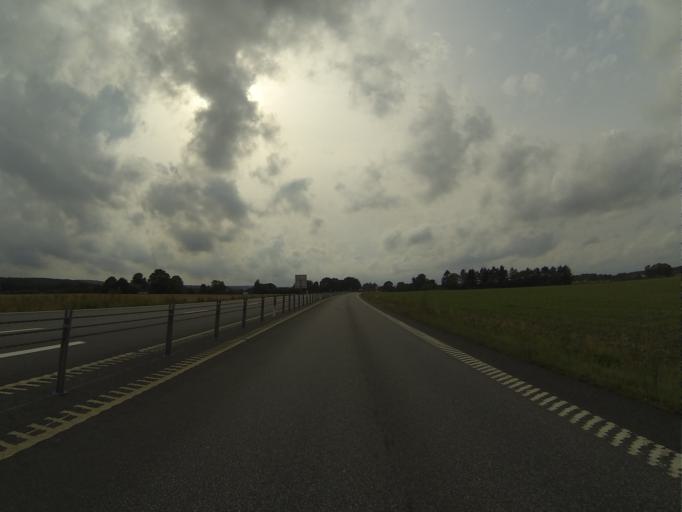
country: SE
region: Skane
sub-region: Kristianstads Kommun
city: Degeberga
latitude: 55.9333
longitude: 14.0231
